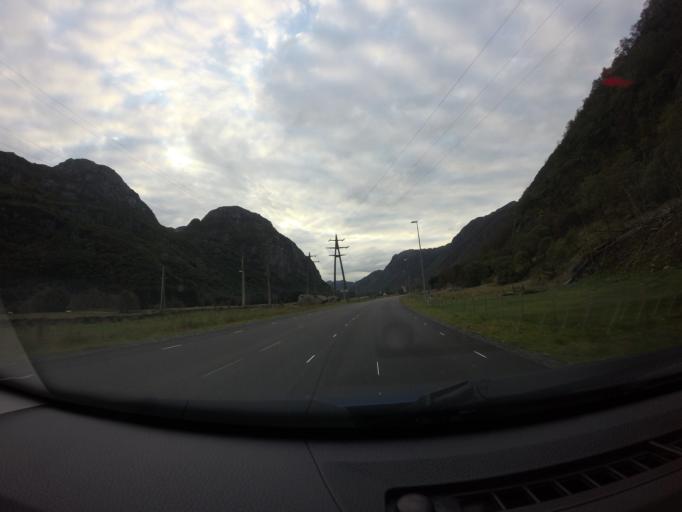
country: NO
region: Rogaland
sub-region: Forsand
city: Forsand
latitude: 58.8308
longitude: 6.1838
